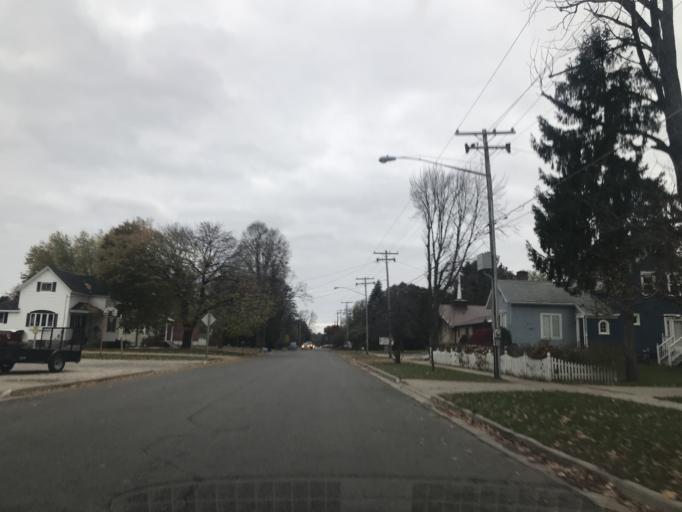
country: US
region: Wisconsin
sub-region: Marinette County
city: Marinette
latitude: 45.0929
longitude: -87.6484
